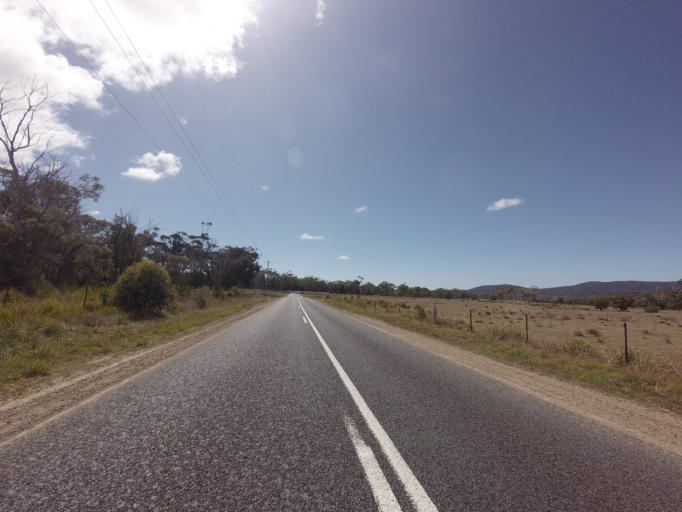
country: AU
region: Tasmania
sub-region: Break O'Day
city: St Helens
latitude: -41.9196
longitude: 148.2433
